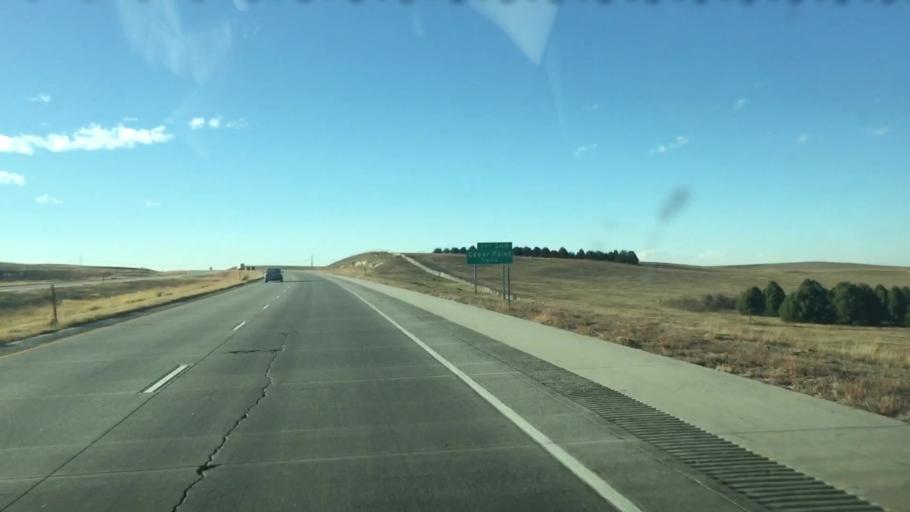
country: US
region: Colorado
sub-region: Lincoln County
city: Limon
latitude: 39.3437
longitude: -103.8472
